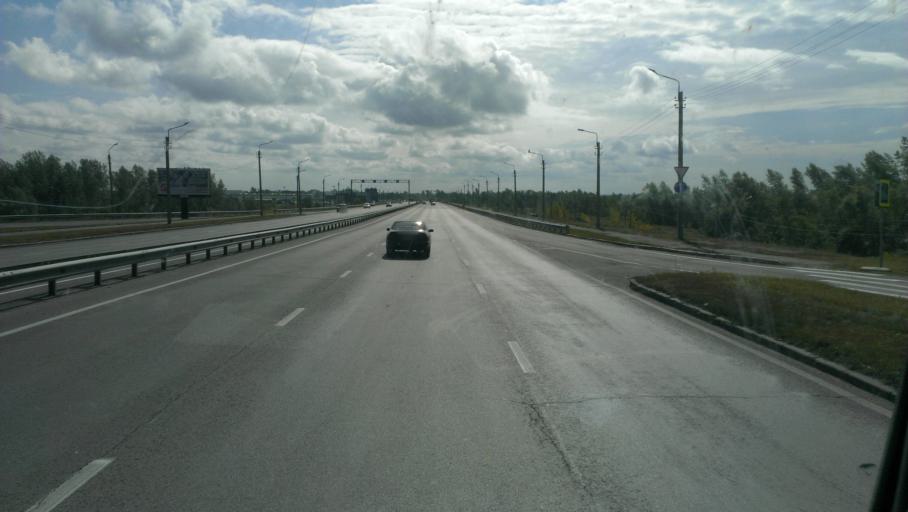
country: RU
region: Altai Krai
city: Zaton
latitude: 53.3194
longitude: 83.8152
